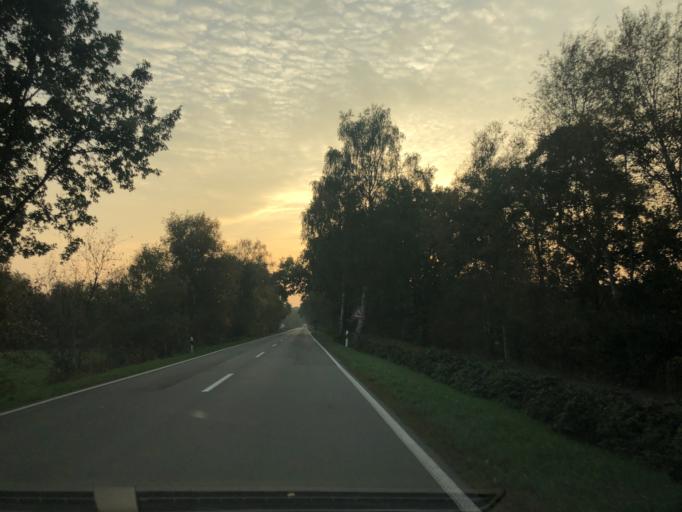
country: DE
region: Lower Saxony
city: Garrel
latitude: 53.0305
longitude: 8.0891
